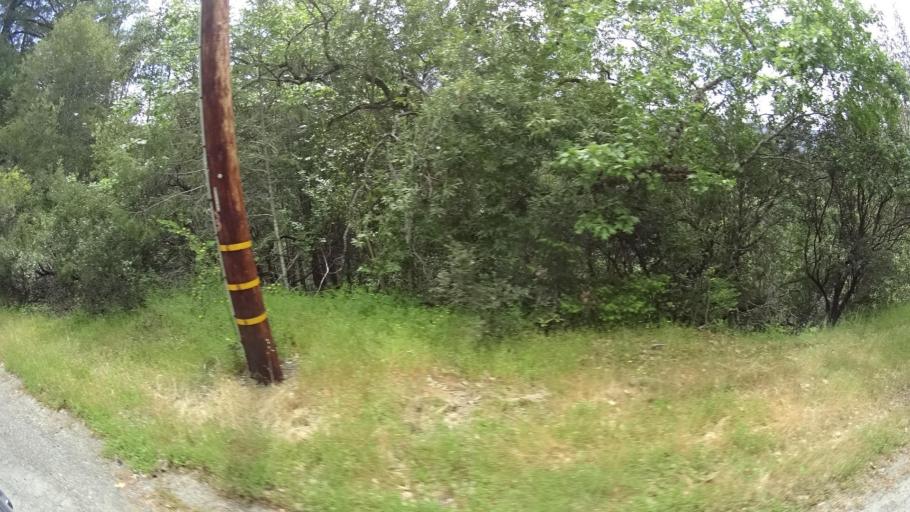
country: US
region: California
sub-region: Humboldt County
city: Redway
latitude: 40.0789
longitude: -123.8188
